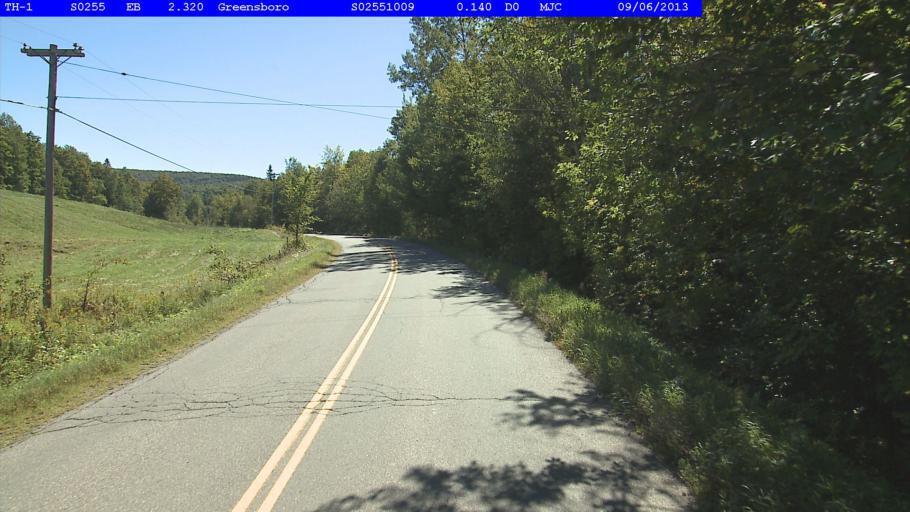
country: US
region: Vermont
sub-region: Caledonia County
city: Hardwick
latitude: 44.6365
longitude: -72.3333
